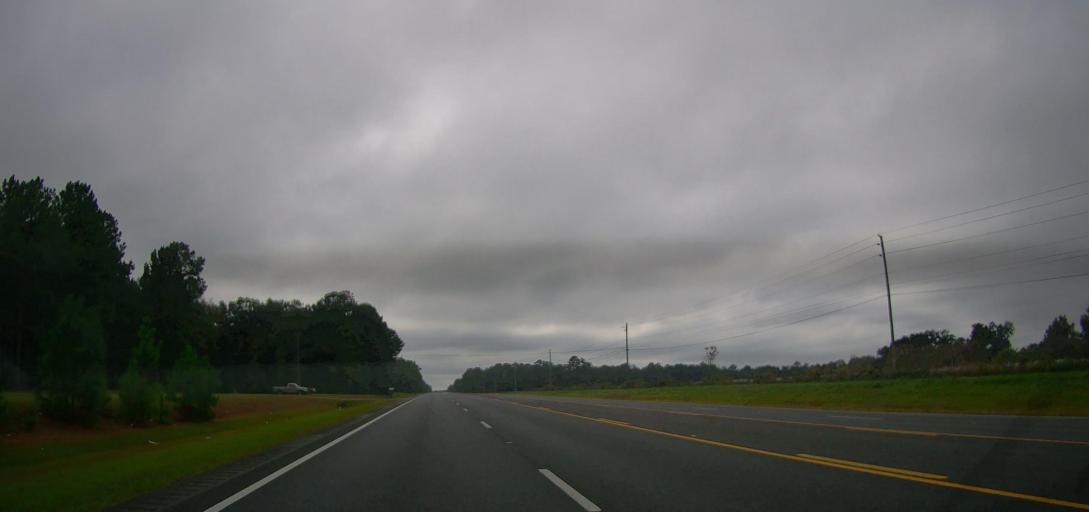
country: US
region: Georgia
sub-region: Thomas County
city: Thomasville
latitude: 30.9165
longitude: -83.9176
